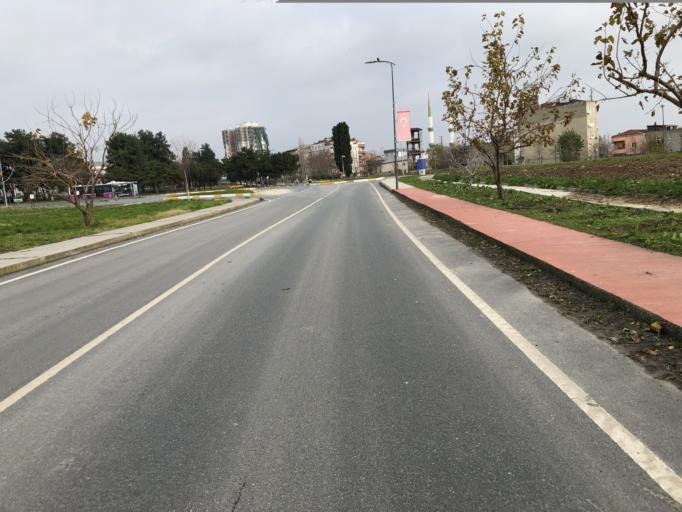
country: TR
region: Istanbul
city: merter keresteciler
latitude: 41.0247
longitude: 28.8937
